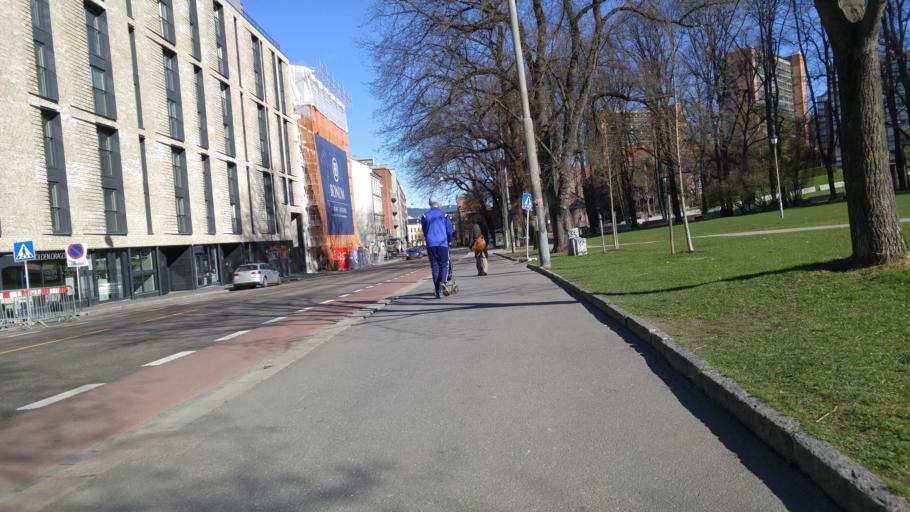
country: NO
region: Oslo
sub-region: Oslo
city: Oslo
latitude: 59.9095
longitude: 10.7685
